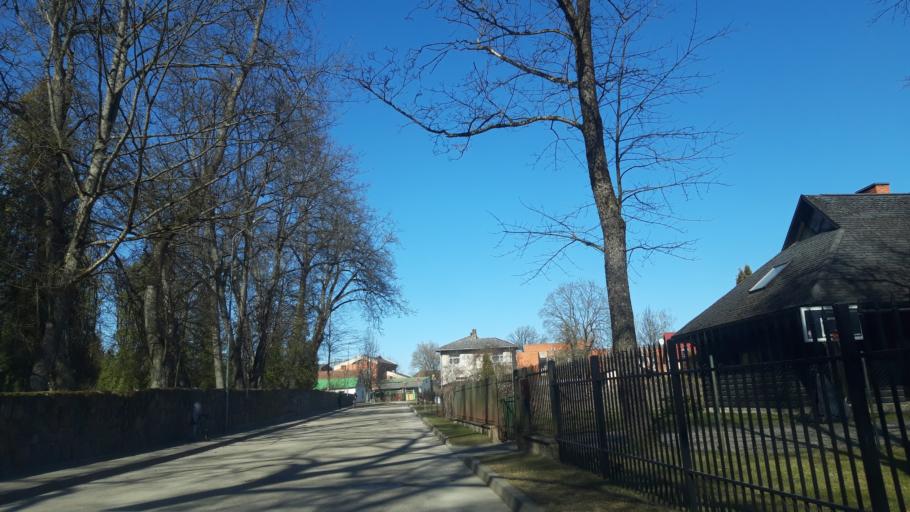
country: LV
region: Valmieras Rajons
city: Valmiera
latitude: 57.5349
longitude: 25.4145
